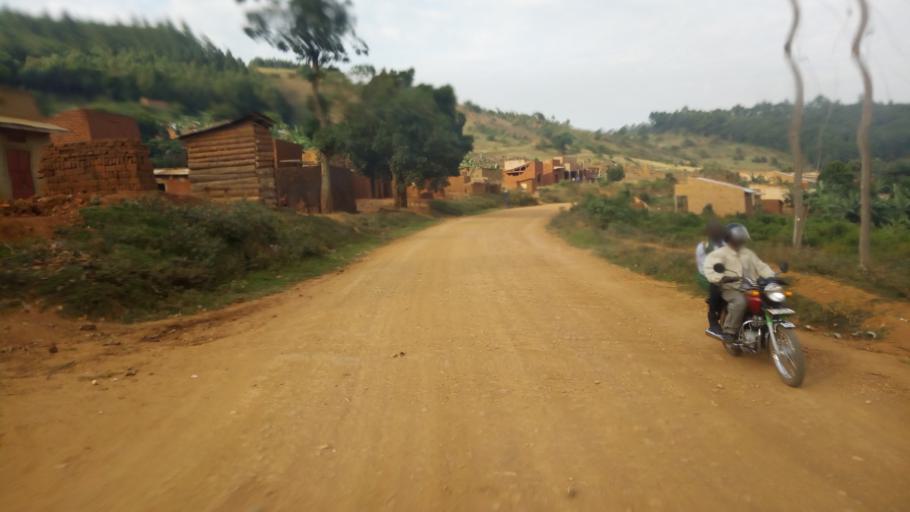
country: UG
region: Western Region
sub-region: Kanungu District
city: Ntungamo
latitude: -0.8293
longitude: 29.6990
